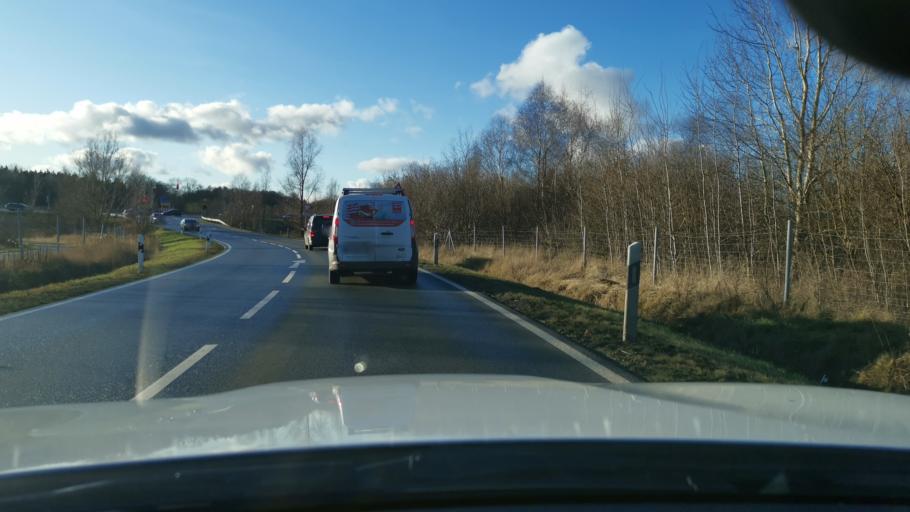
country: DE
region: Mecklenburg-Vorpommern
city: Tessin
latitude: 54.0409
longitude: 12.4107
